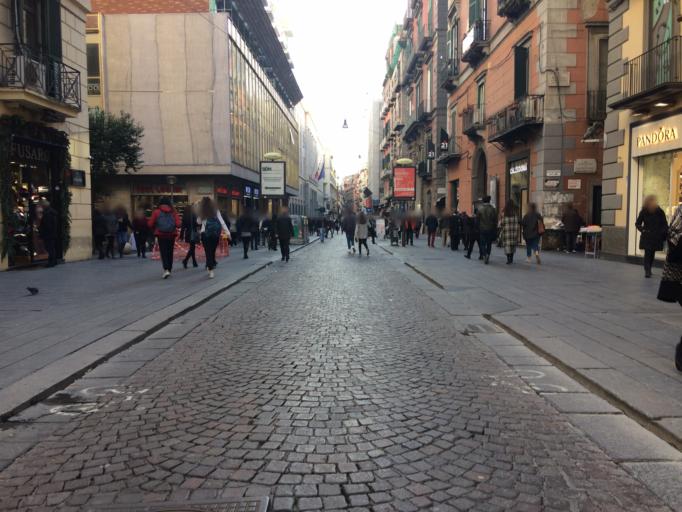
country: IT
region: Campania
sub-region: Provincia di Napoli
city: Napoli
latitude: 40.8417
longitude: 14.2488
